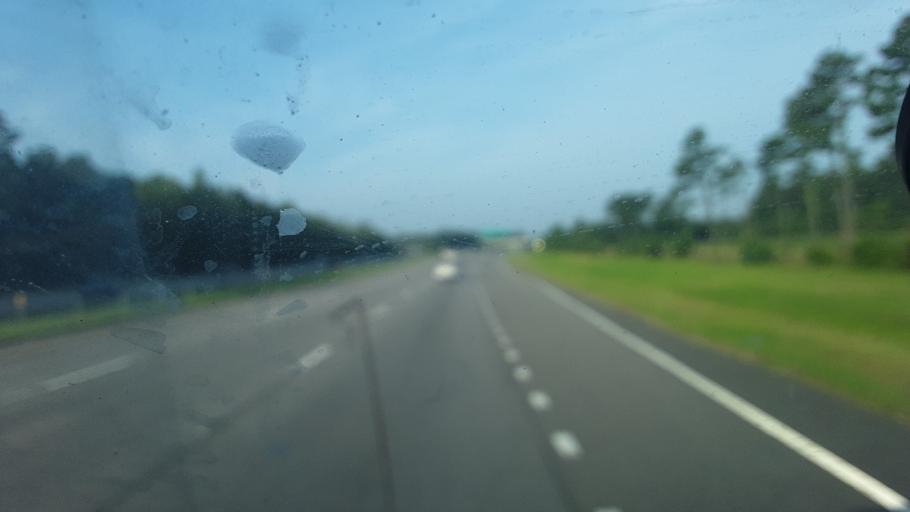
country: US
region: South Carolina
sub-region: Horry County
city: Myrtle Beach
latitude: 33.7573
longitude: -78.8461
